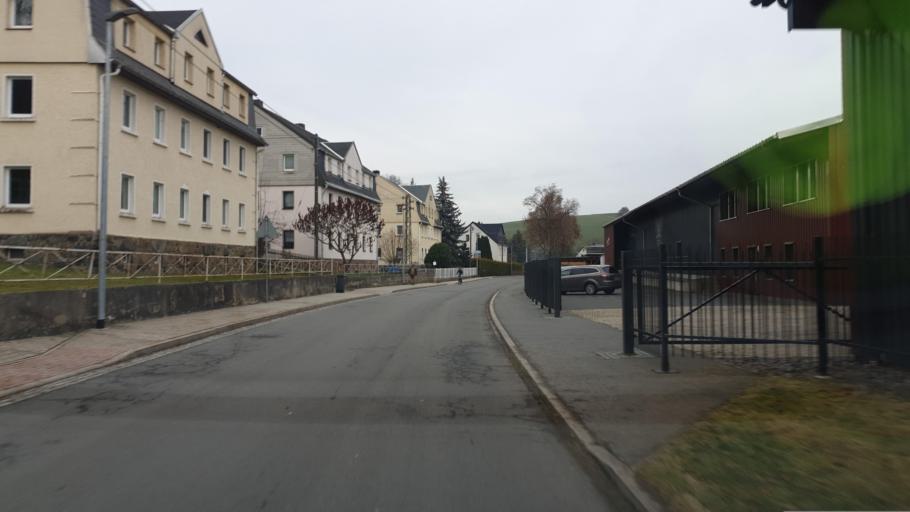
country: DE
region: Saxony
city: Mulda
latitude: 50.8064
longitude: 13.4065
